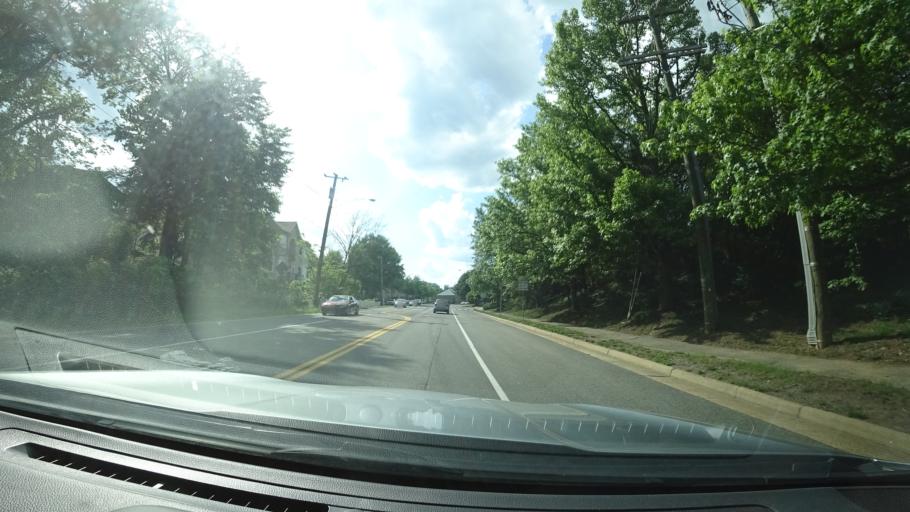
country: US
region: Virginia
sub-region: Fairfax County
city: McLean
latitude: 38.9306
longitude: -77.1717
